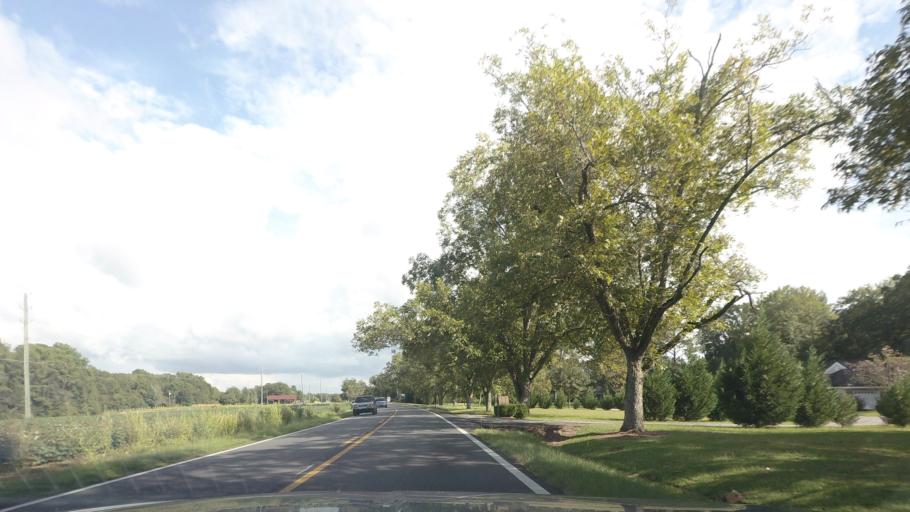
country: US
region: Georgia
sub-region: Peach County
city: Byron
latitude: 32.6383
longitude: -83.7370
